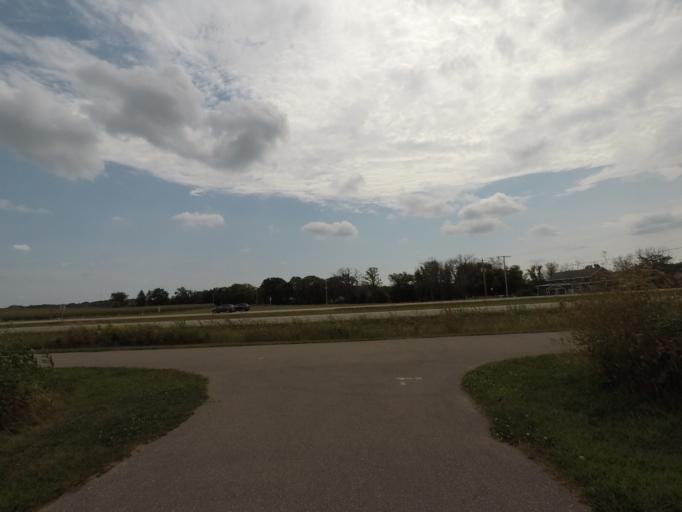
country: US
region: Wisconsin
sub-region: Jefferson County
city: Lake Koshkonong
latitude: 42.8470
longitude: -88.9188
